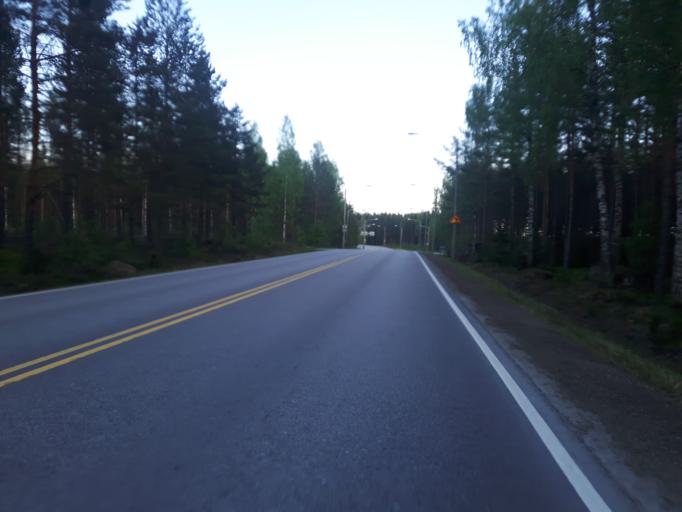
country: FI
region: Uusimaa
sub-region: Loviisa
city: Perna
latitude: 60.4543
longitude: 26.0948
